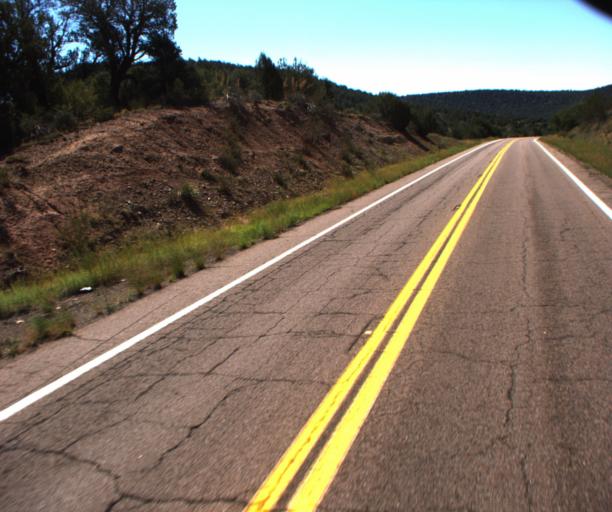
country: US
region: Arizona
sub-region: Navajo County
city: Cibecue
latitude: 33.9145
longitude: -110.3633
